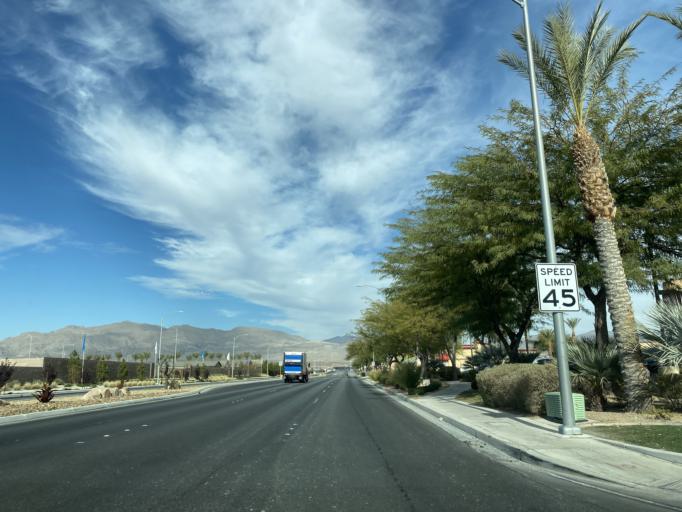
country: US
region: Nevada
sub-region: Clark County
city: Nellis Air Force Base
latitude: 36.2773
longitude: -115.1168
